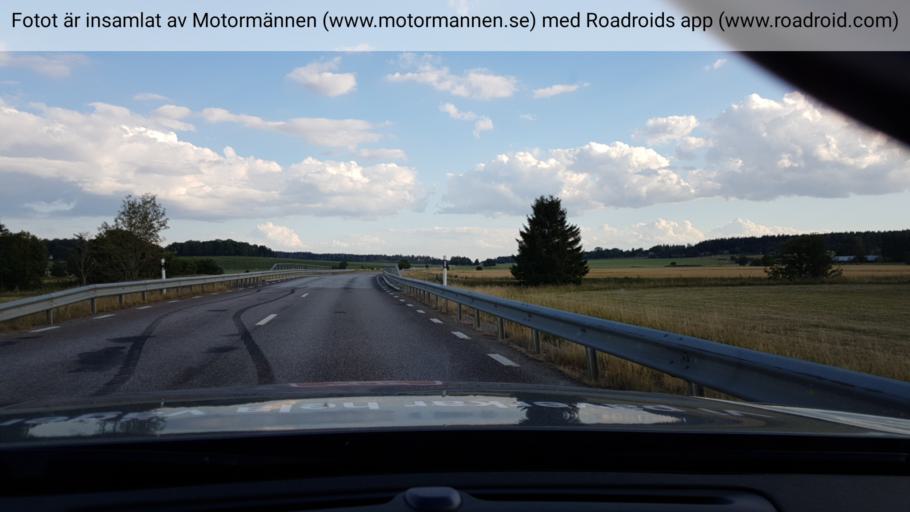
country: SE
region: Uppsala
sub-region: Heby Kommun
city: Morgongava
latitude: 59.8301
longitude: 16.9270
